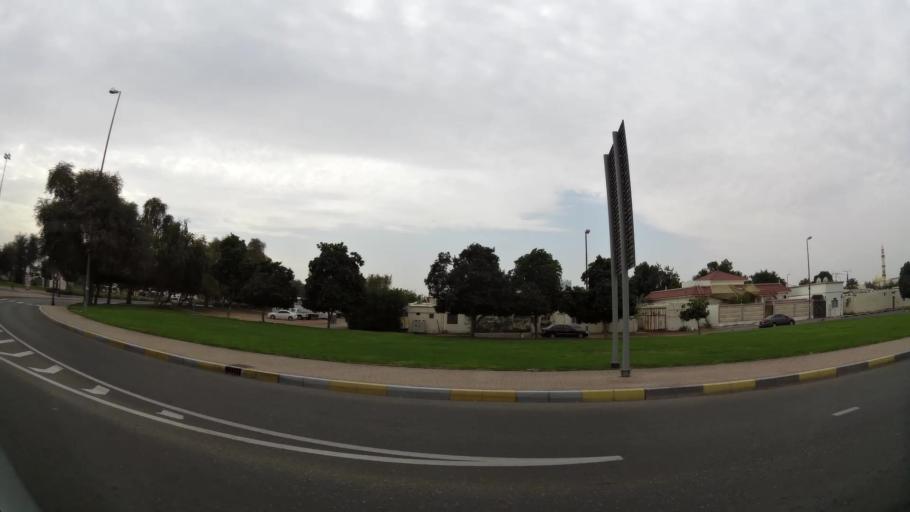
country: AE
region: Abu Dhabi
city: Al Ain
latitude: 24.2246
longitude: 55.7374
